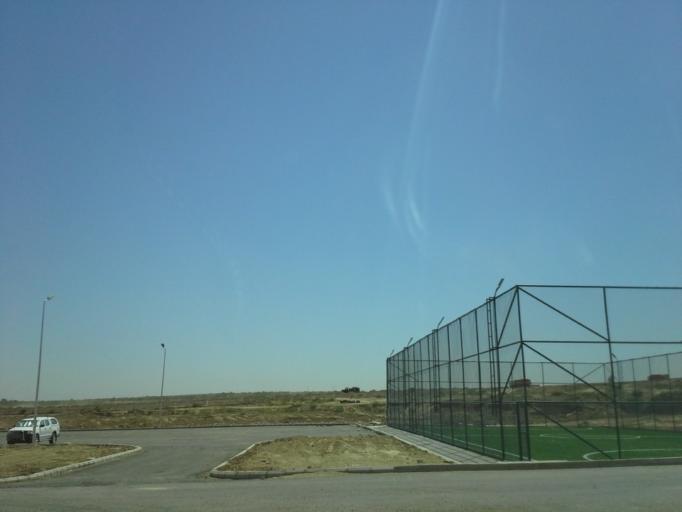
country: TM
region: Ahal
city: Ashgabat
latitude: 37.8859
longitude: 58.4121
